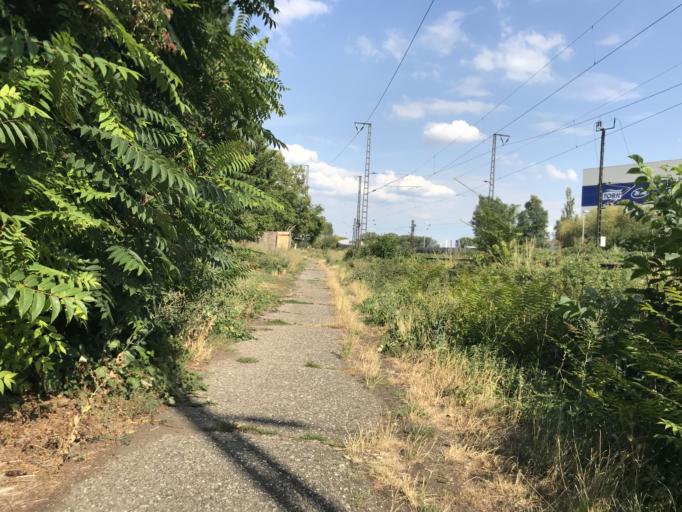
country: DE
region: Hesse
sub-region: Regierungsbezirk Darmstadt
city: Hochheim am Main
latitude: 50.0064
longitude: 8.3140
